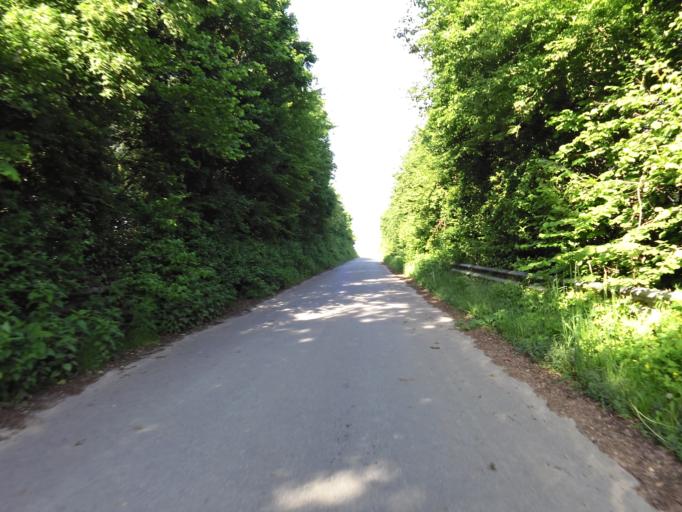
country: DE
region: Hesse
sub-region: Regierungsbezirk Darmstadt
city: Burstadt
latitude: 49.6277
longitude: 8.4684
